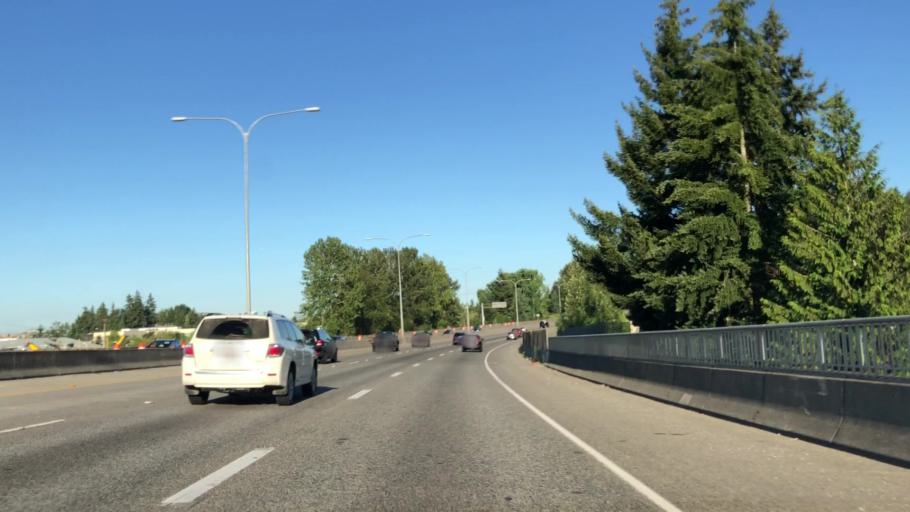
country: US
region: Washington
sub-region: King County
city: Bellevue
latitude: 47.6294
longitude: -122.1510
